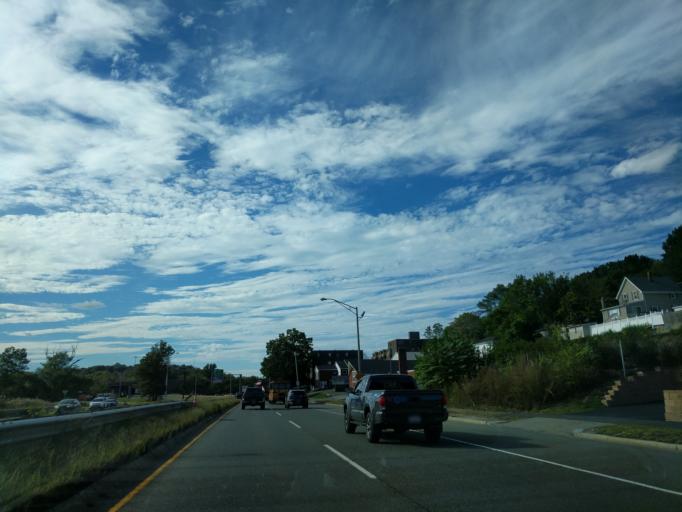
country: US
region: Massachusetts
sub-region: Suffolk County
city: Revere
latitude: 42.4059
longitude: -71.0215
